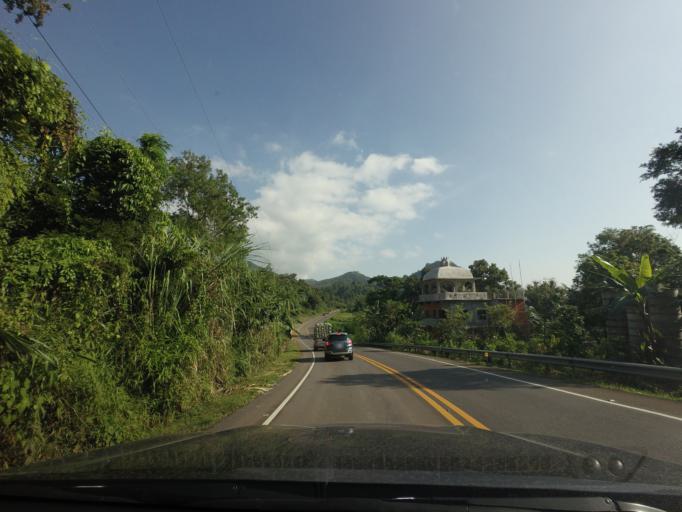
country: TH
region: Phetchabun
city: Lom Kao
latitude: 16.8697
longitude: 101.1436
